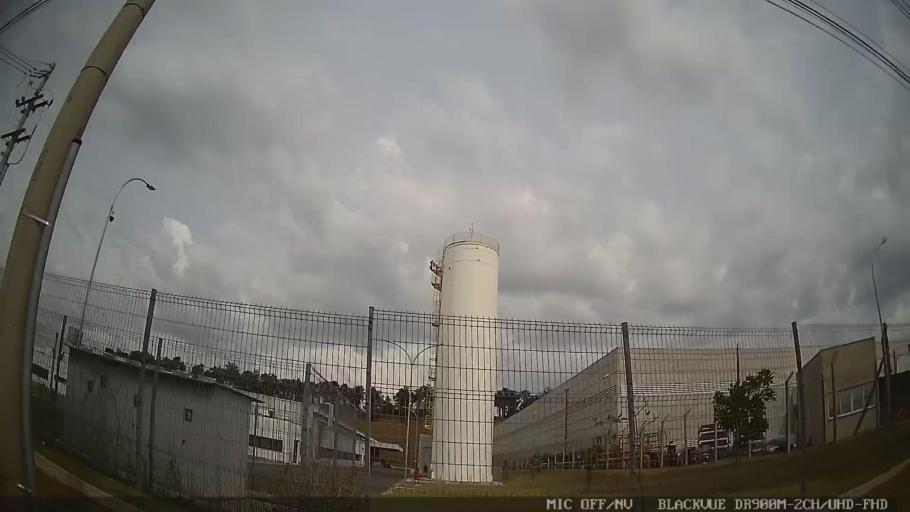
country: BR
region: Sao Paulo
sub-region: Indaiatuba
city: Indaiatuba
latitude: -23.1120
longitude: -47.2789
